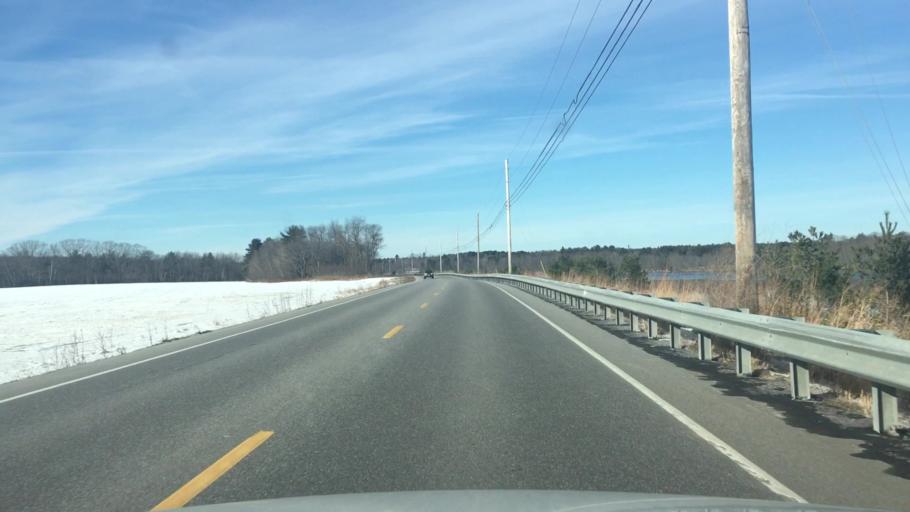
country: US
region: Maine
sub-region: Androscoggin County
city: Lisbon
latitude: 43.9906
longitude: -70.1390
